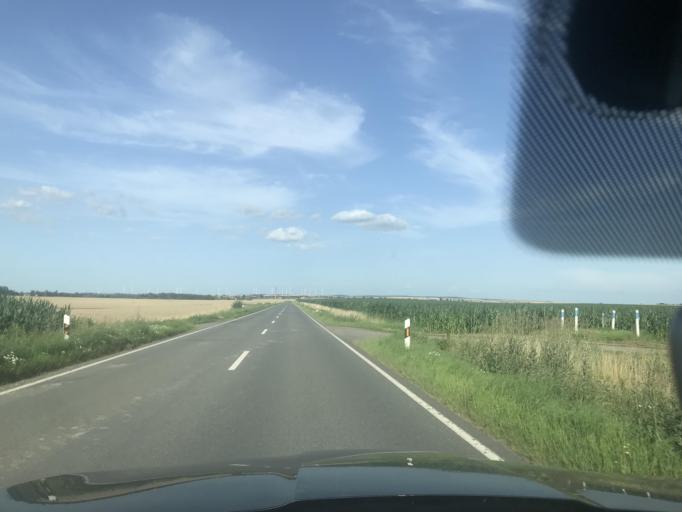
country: DE
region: Saxony-Anhalt
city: Harsleben
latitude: 51.8705
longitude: 11.1260
